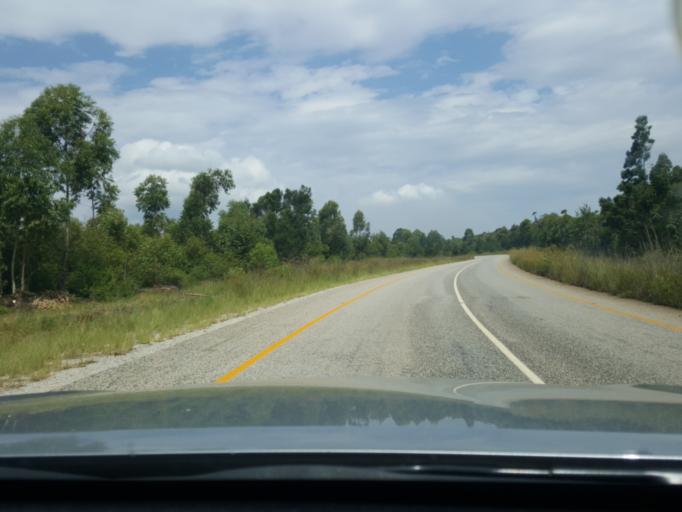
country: ZA
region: Mpumalanga
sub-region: Ehlanzeni District
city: White River
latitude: -25.1873
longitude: 30.9036
